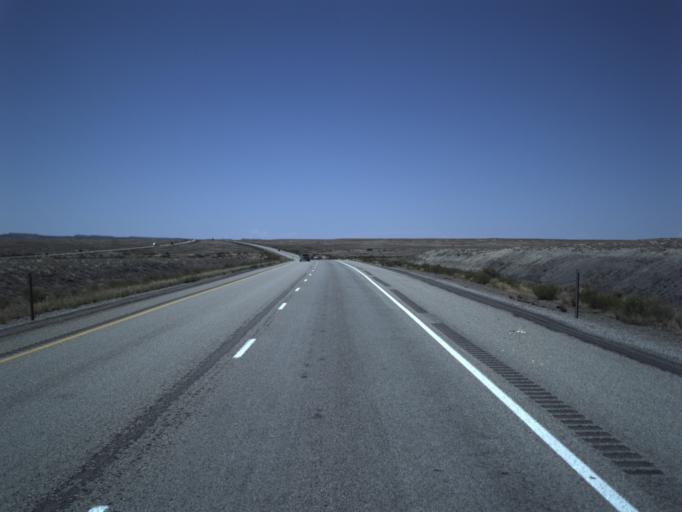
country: US
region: Utah
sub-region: Grand County
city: Moab
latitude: 38.9710
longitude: -109.3648
